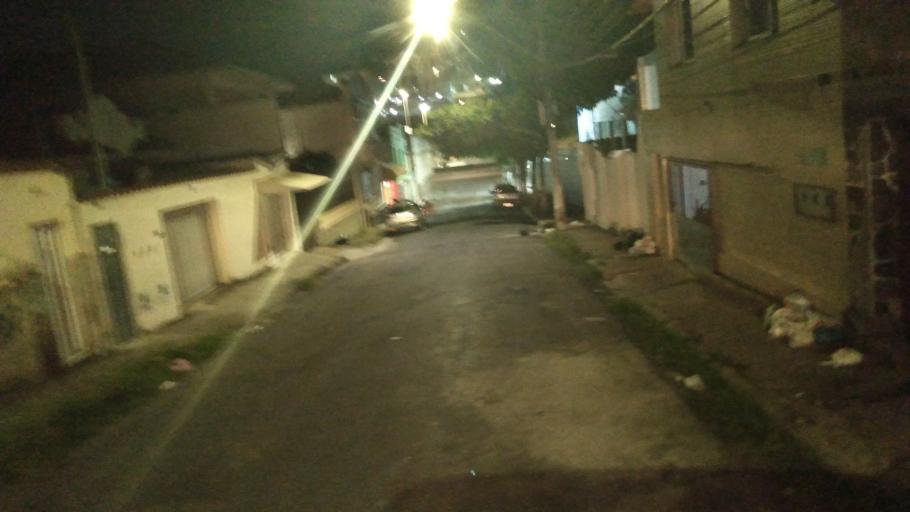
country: BR
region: Minas Gerais
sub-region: Belo Horizonte
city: Belo Horizonte
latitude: -19.9061
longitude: -43.9448
